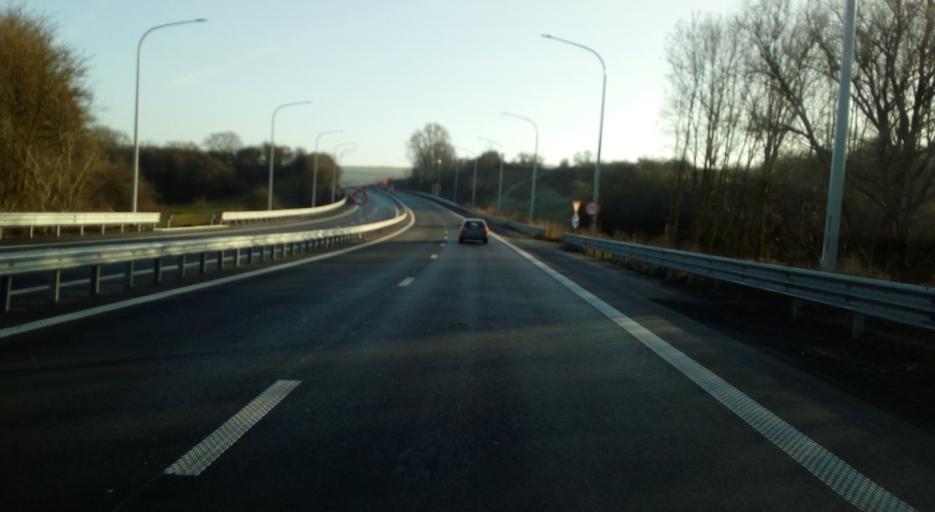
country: BE
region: Wallonia
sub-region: Province de Namur
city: Walcourt
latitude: 50.2831
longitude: 4.4823
